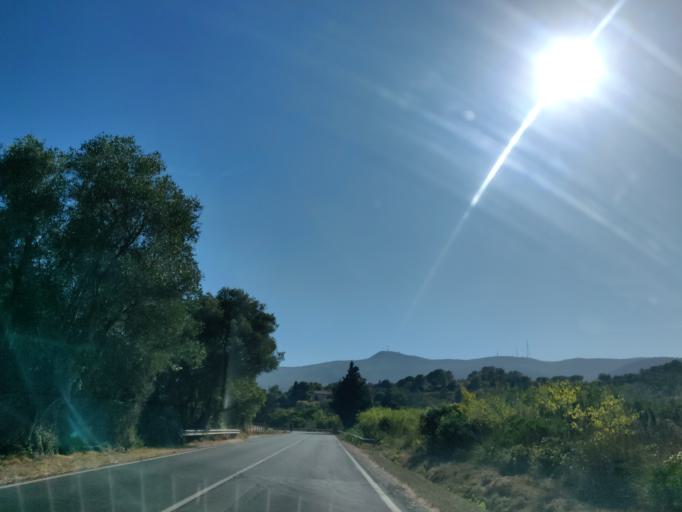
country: IT
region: Tuscany
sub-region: Provincia di Grosseto
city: Porto Ercole
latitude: 42.4098
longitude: 11.2016
